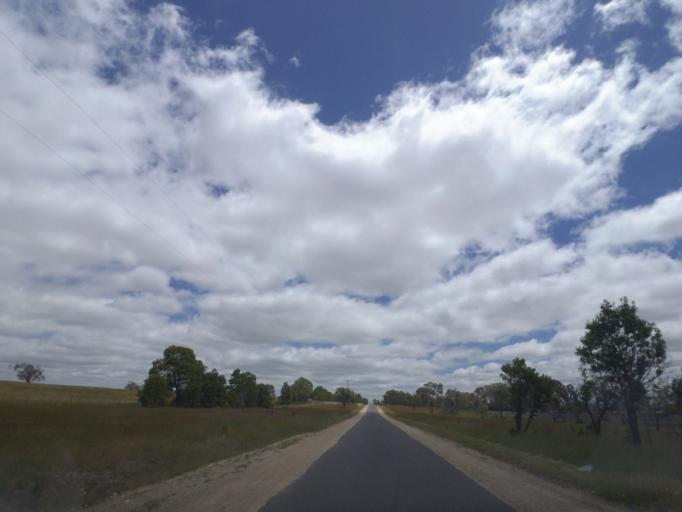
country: AU
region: Victoria
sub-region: Moorabool
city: Bacchus Marsh
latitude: -37.6294
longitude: 144.2662
